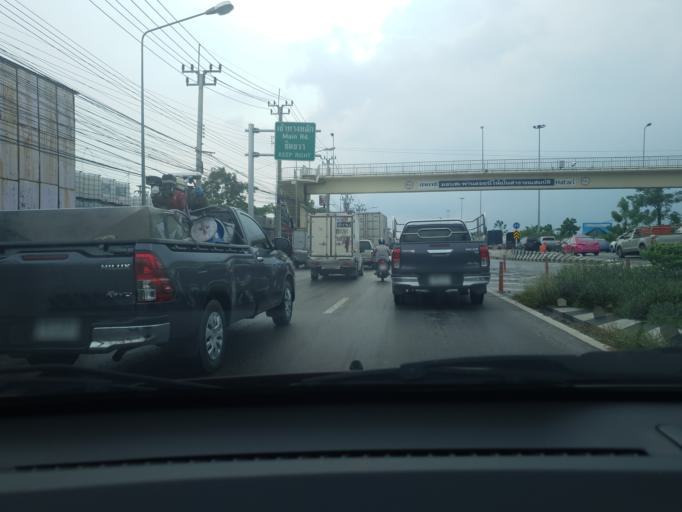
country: TH
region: Bangkok
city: Bang Bon
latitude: 13.6198
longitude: 100.3875
